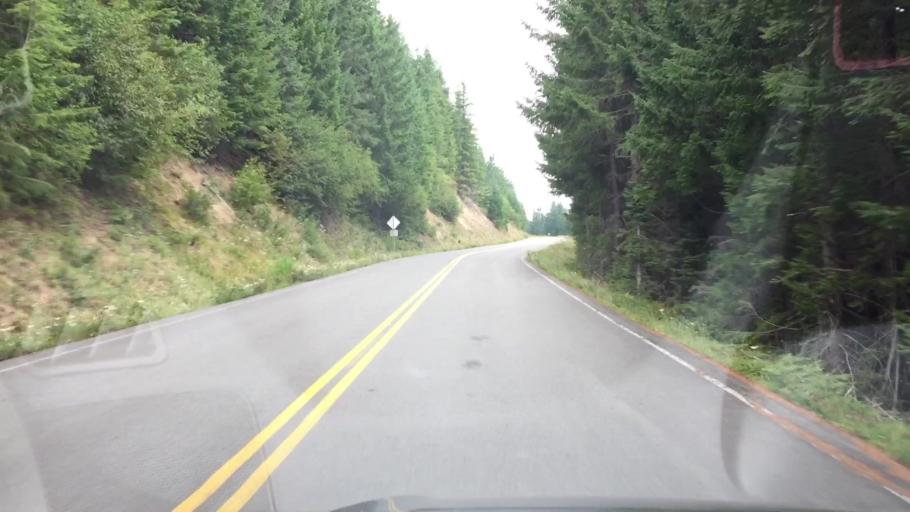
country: US
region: Washington
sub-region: Klickitat County
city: White Salmon
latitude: 46.1499
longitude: -121.6275
